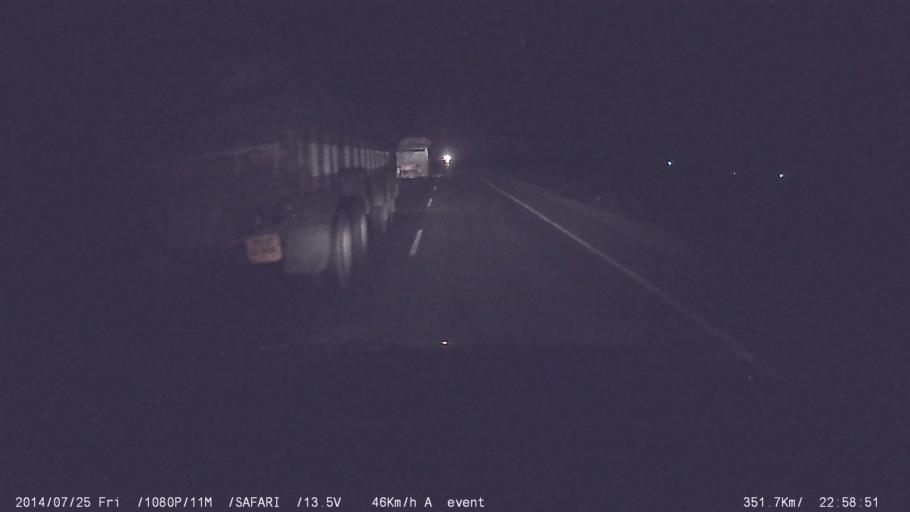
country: IN
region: Tamil Nadu
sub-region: Coimbatore
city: Singanallur
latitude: 10.9634
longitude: 77.0303
